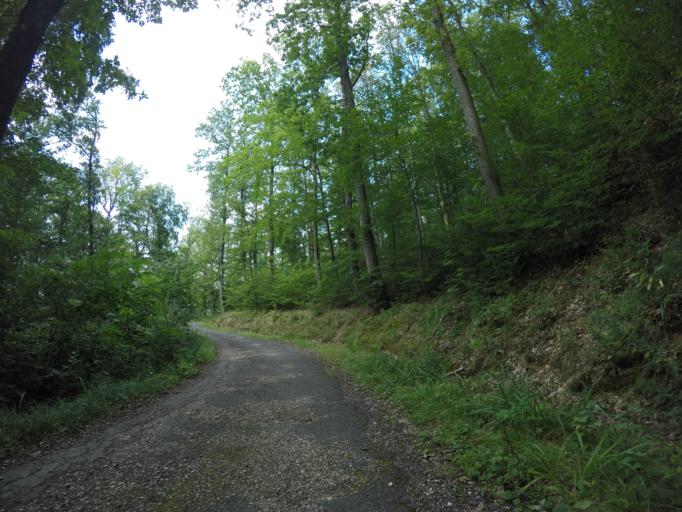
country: DE
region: Baden-Wuerttemberg
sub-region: Tuebingen Region
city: Reutlingen
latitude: 48.4657
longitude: 9.1962
